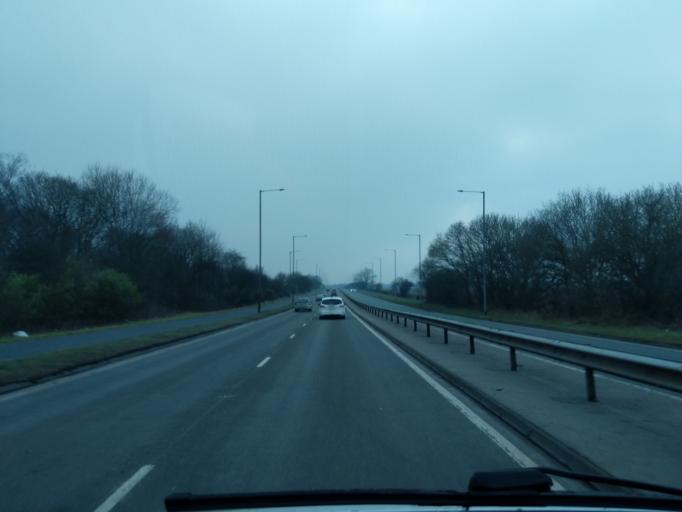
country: GB
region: England
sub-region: St. Helens
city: Haydock
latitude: 53.4725
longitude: -2.6939
